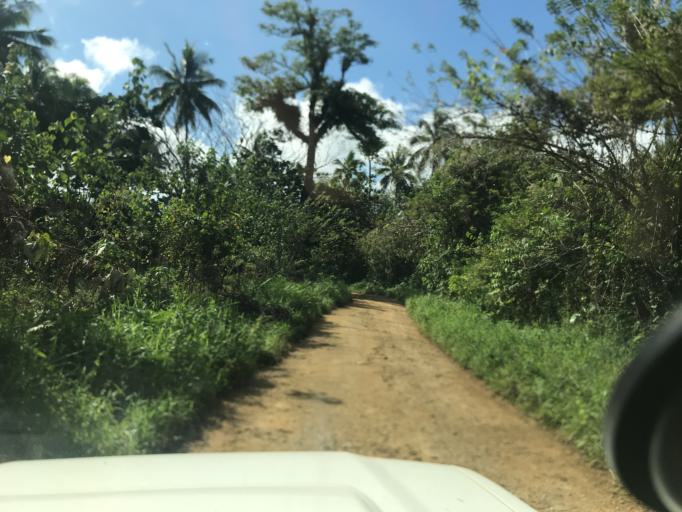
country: VU
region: Sanma
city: Luganville
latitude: -15.4639
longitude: 167.0726
